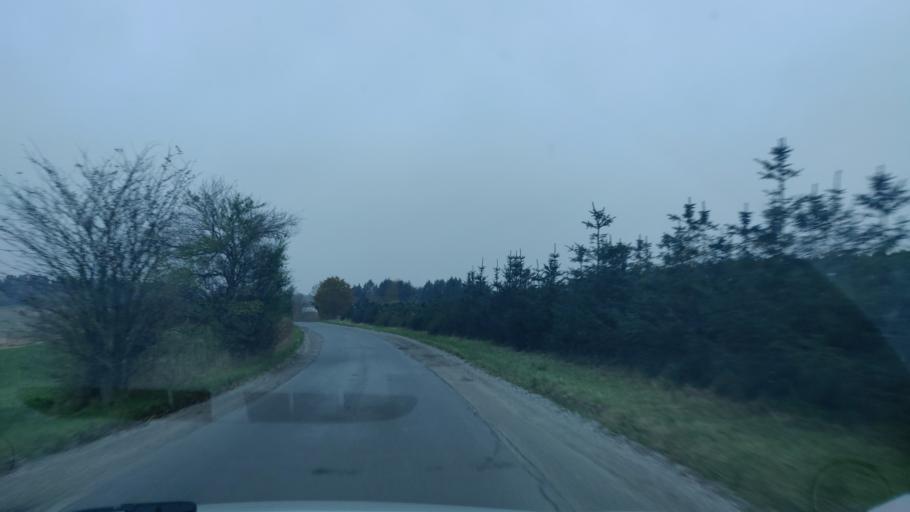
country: DK
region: South Denmark
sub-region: Kolding Kommune
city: Kolding
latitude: 55.5668
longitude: 9.4294
